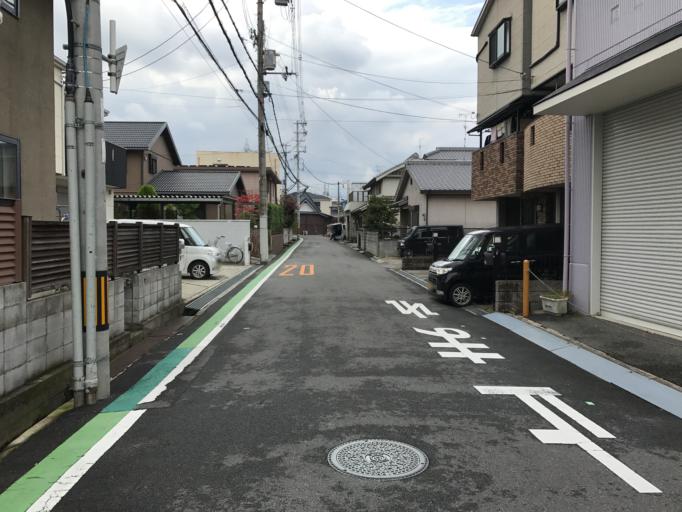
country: JP
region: Osaka
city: Kashihara
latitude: 34.5663
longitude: 135.6157
